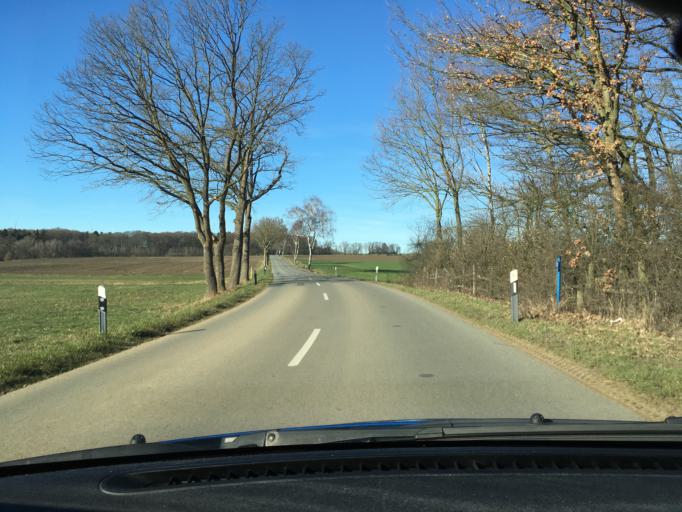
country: DE
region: Lower Saxony
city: Schwienau
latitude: 52.9686
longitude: 10.4574
